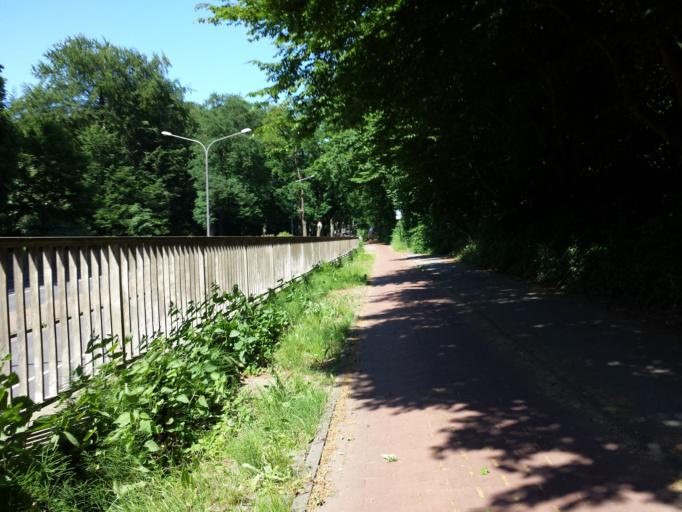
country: DE
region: Bremen
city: Bremen
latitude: 53.1019
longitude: 8.8388
